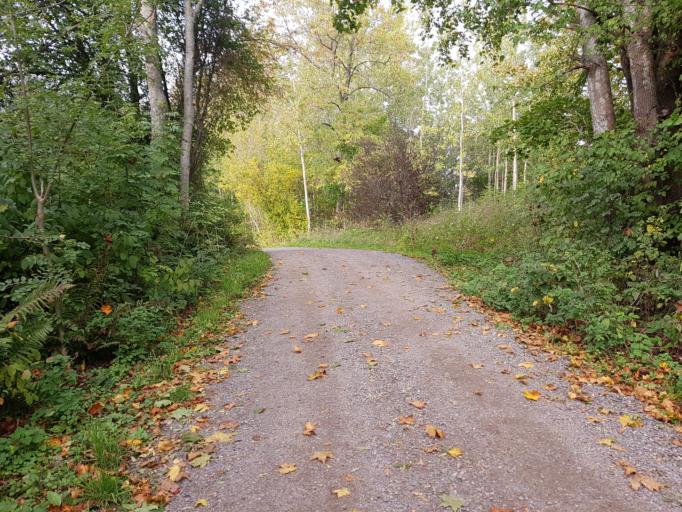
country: FI
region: Uusimaa
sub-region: Helsinki
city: Helsinki
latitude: 60.1391
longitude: 24.9973
